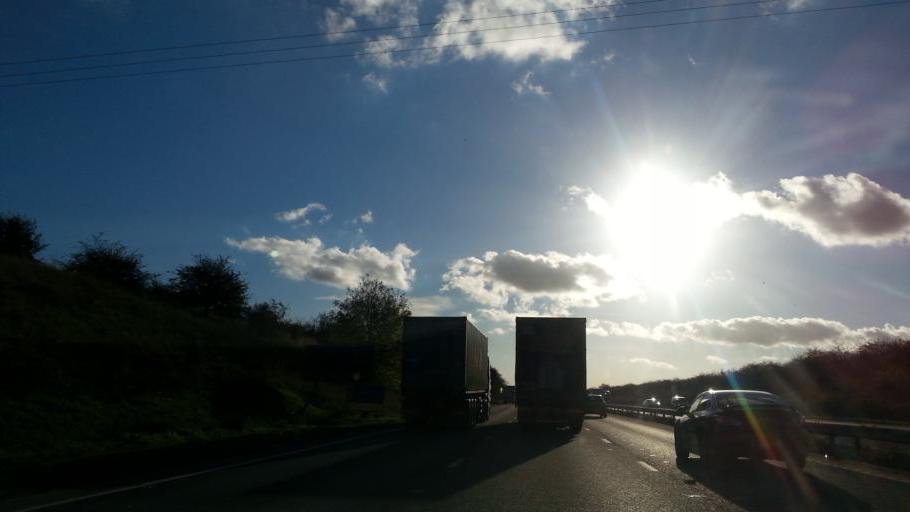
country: GB
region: England
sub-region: Suffolk
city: Exning
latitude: 52.2351
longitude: 0.3314
